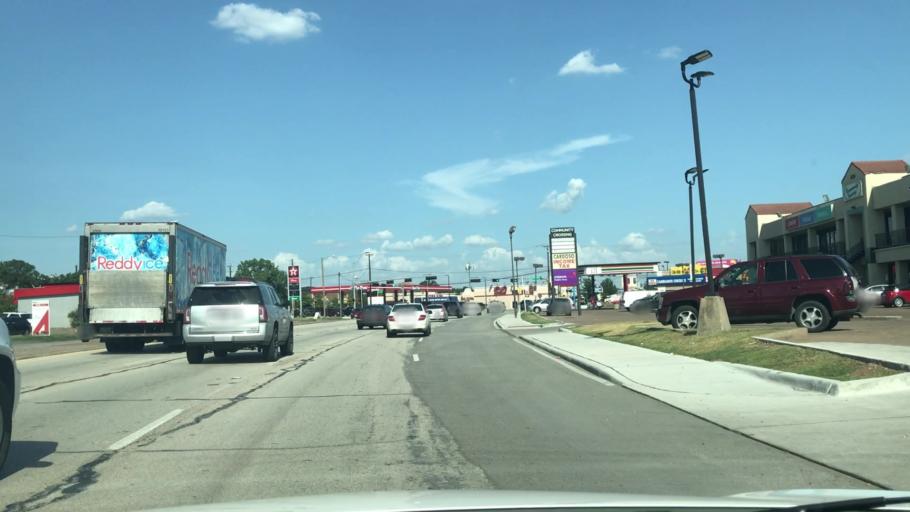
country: US
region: Texas
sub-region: Dallas County
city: Farmers Branch
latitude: 32.8582
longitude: -96.8755
